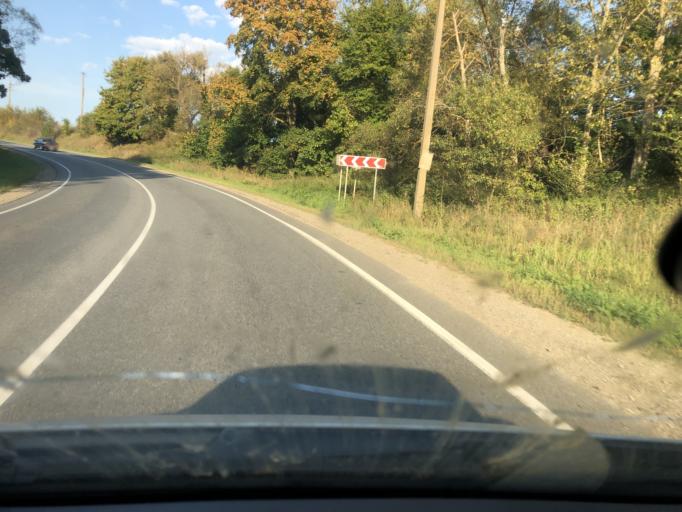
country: RU
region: Kaluga
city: Peremyshl'
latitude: 54.2283
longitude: 36.0530
